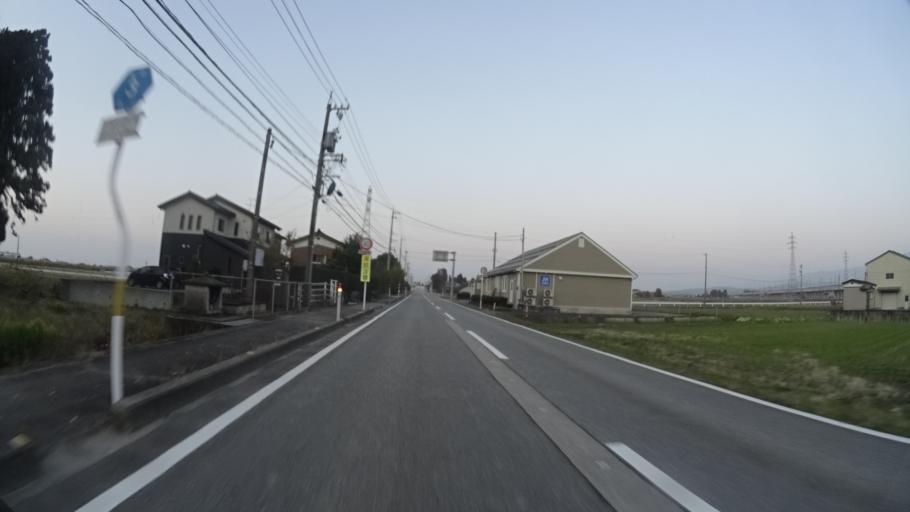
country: JP
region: Toyama
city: Namerikawa
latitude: 36.7622
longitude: 137.3748
